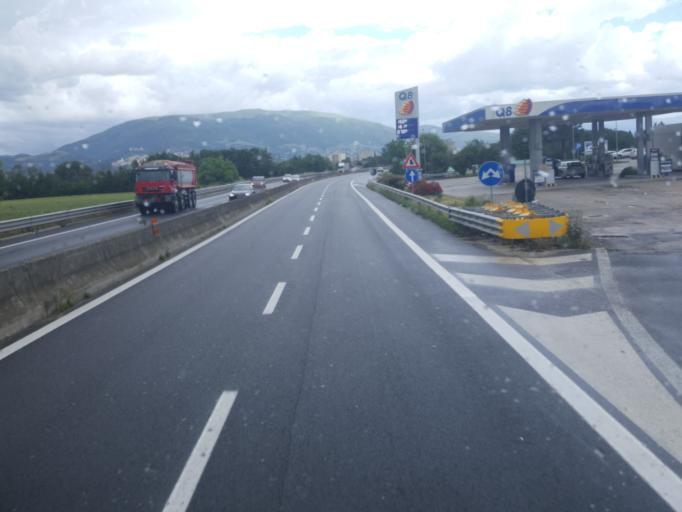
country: IT
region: Umbria
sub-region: Provincia di Perugia
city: Ospedalicchio
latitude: 43.0718
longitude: 12.5236
